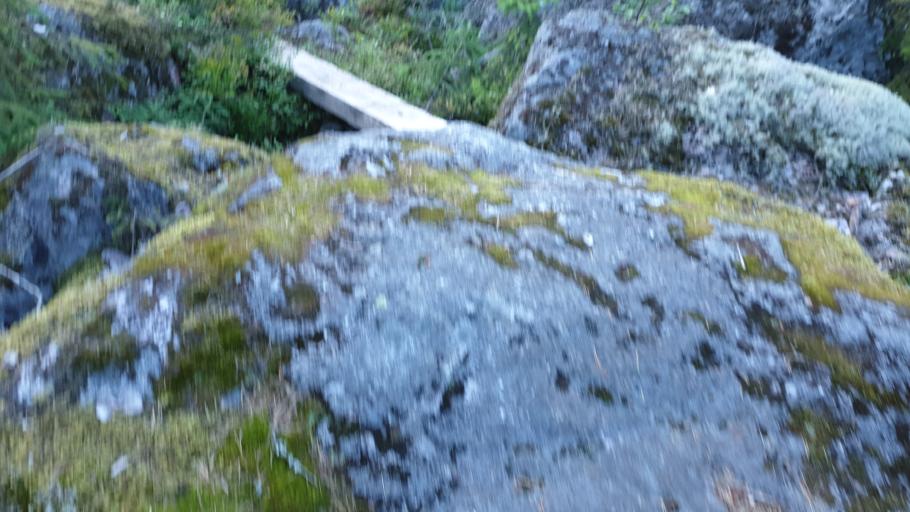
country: SE
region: Gaevleborg
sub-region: Soderhamns Kommun
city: Marielund
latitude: 61.4230
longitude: 17.1537
